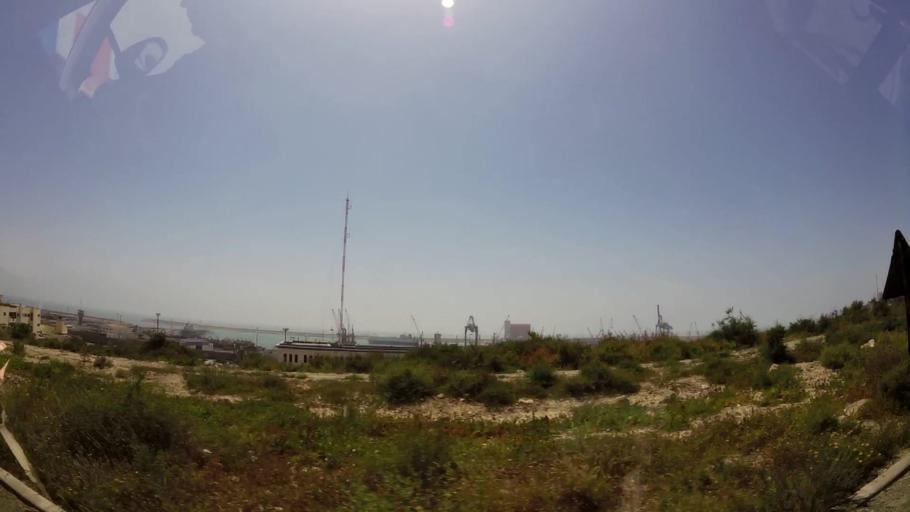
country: MA
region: Souss-Massa-Draa
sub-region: Agadir-Ida-ou-Tnan
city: Agadir
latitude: 30.4305
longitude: -9.6349
